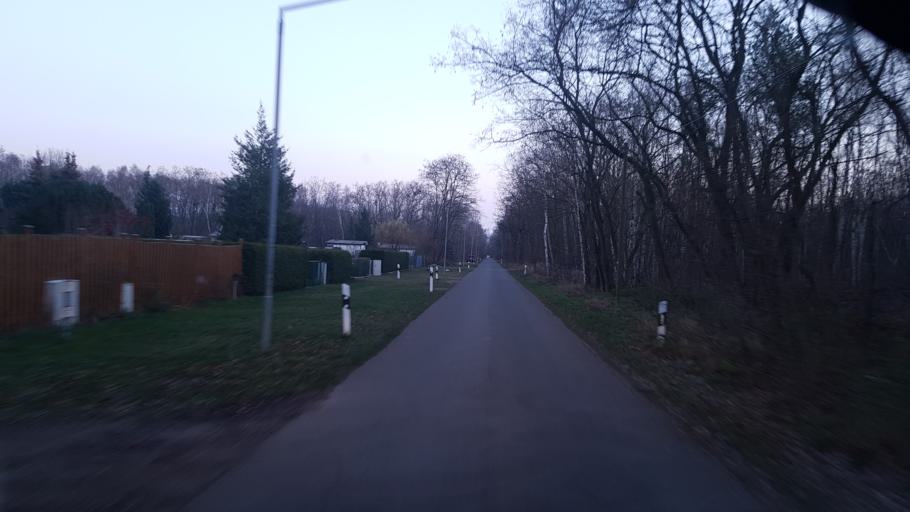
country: DE
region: Brandenburg
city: Lauchhammer
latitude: 51.5192
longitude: 13.7409
